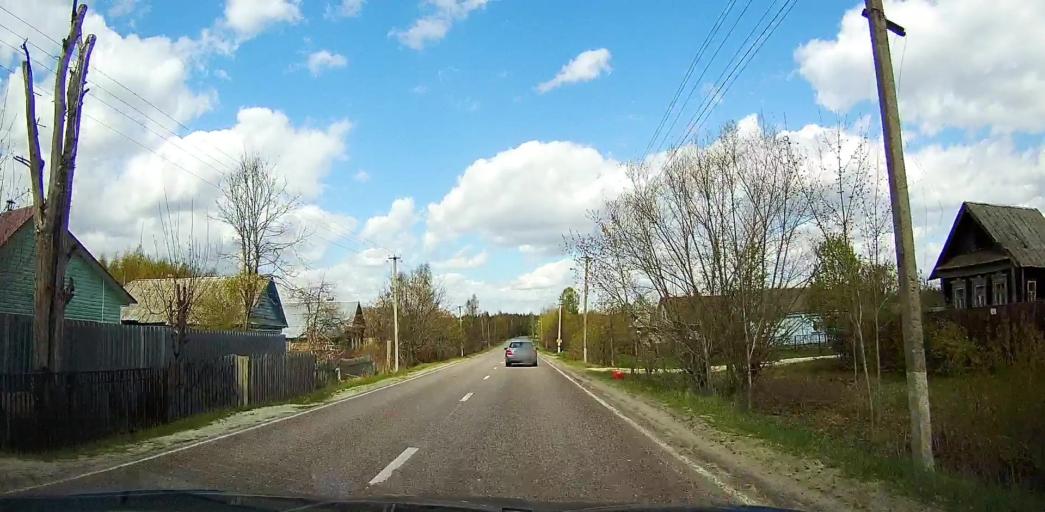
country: RU
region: Moskovskaya
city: Davydovo
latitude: 55.5865
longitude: 38.8290
